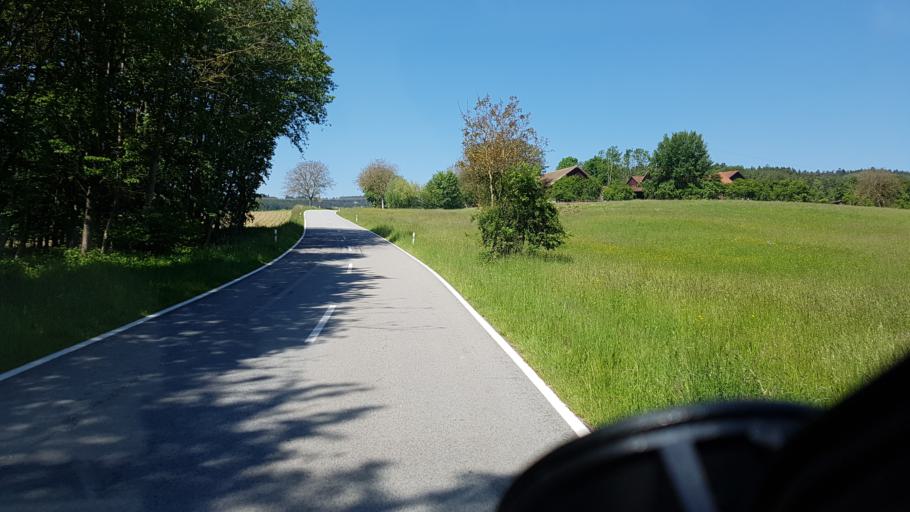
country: DE
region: Bavaria
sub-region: Lower Bavaria
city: Stubenberg
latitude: 48.2940
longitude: 13.0695
